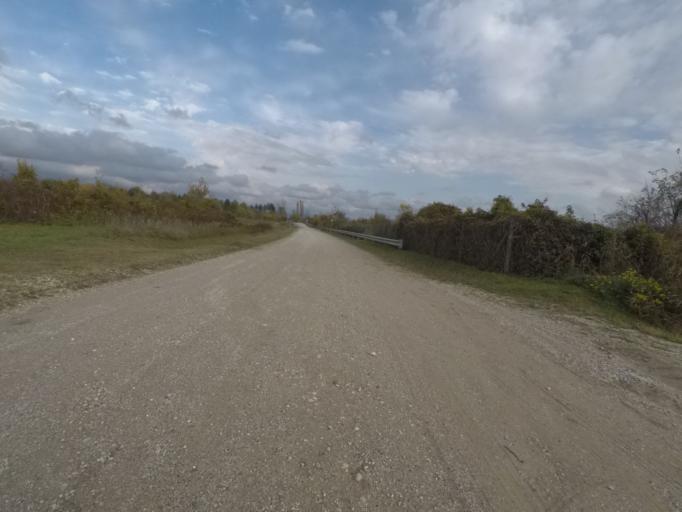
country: IT
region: Friuli Venezia Giulia
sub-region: Provincia di Udine
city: Pradamano
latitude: 46.0442
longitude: 13.2738
